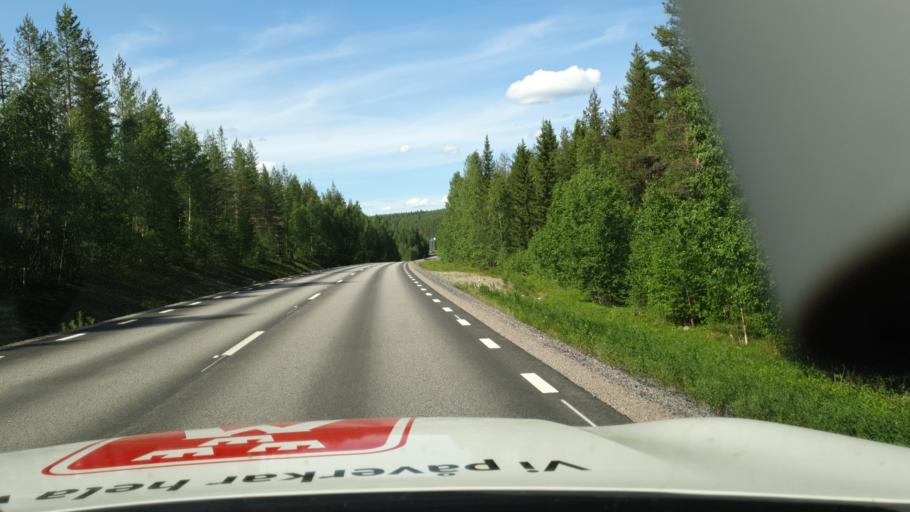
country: SE
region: Vaesterbotten
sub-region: Skelleftea Kommun
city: Boliden
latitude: 64.8906
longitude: 20.3770
